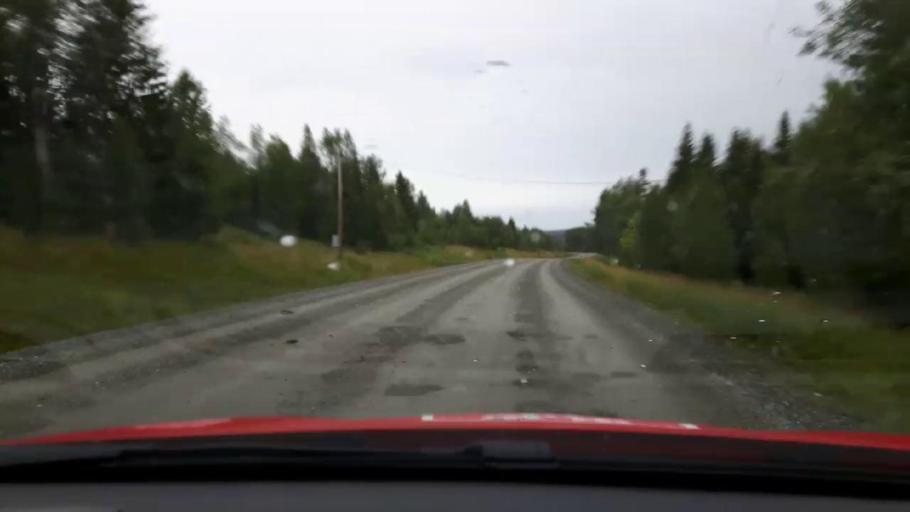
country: SE
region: Jaemtland
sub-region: Are Kommun
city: Are
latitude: 63.4571
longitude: 12.6417
